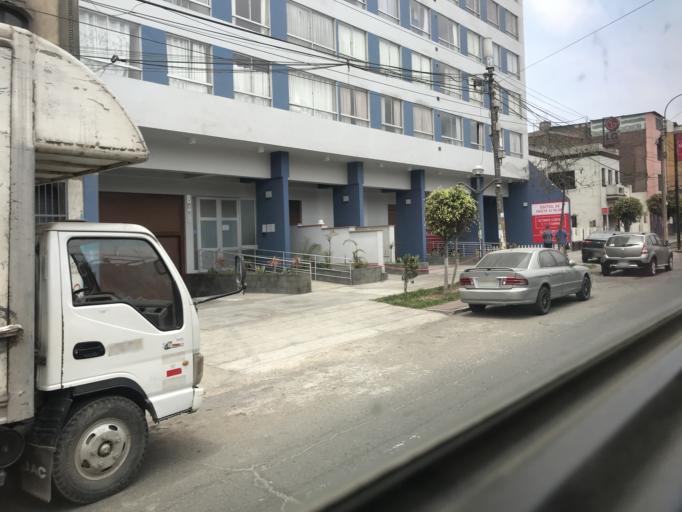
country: PE
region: Lima
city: Lima
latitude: -12.0567
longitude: -77.0472
